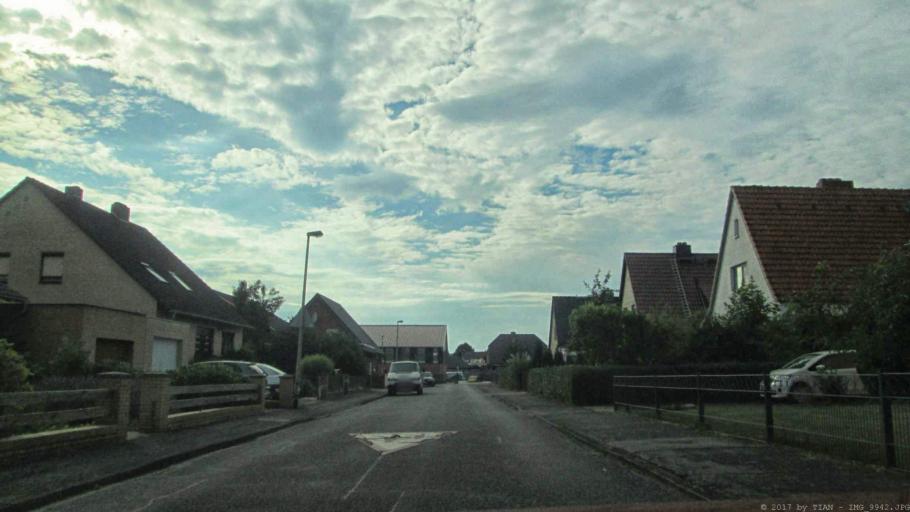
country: DE
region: Lower Saxony
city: Wolfsburg
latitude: 52.3948
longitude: 10.7317
